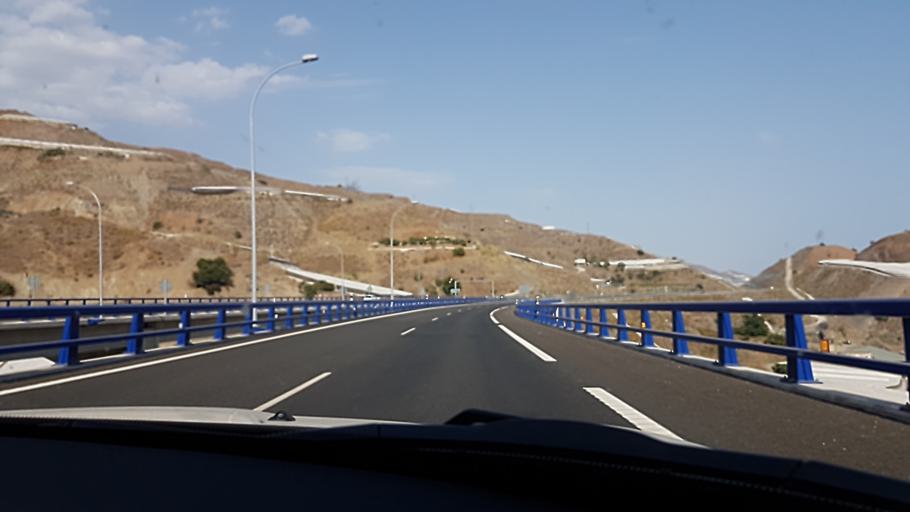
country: ES
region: Andalusia
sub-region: Provincia de Granada
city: Polopos
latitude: 36.7516
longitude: -3.2938
